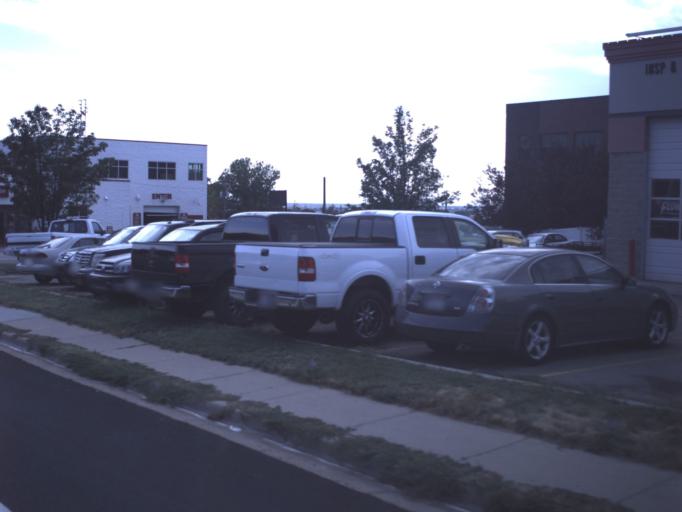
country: US
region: Utah
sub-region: Davis County
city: Woods Cross
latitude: 40.8599
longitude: -111.8978
